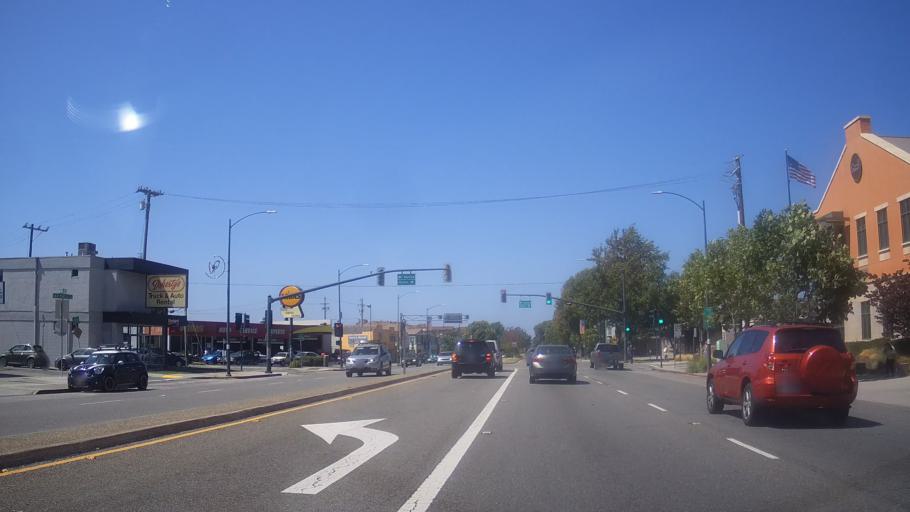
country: US
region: California
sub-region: Contra Costa County
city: El Cerrito
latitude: 37.9152
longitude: -122.3112
